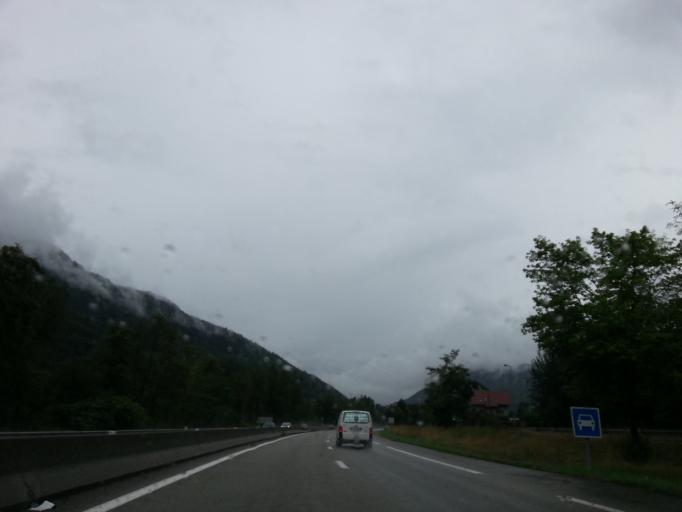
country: FR
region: Rhone-Alpes
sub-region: Departement de la Savoie
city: Marthod
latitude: 45.7362
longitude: 6.4232
